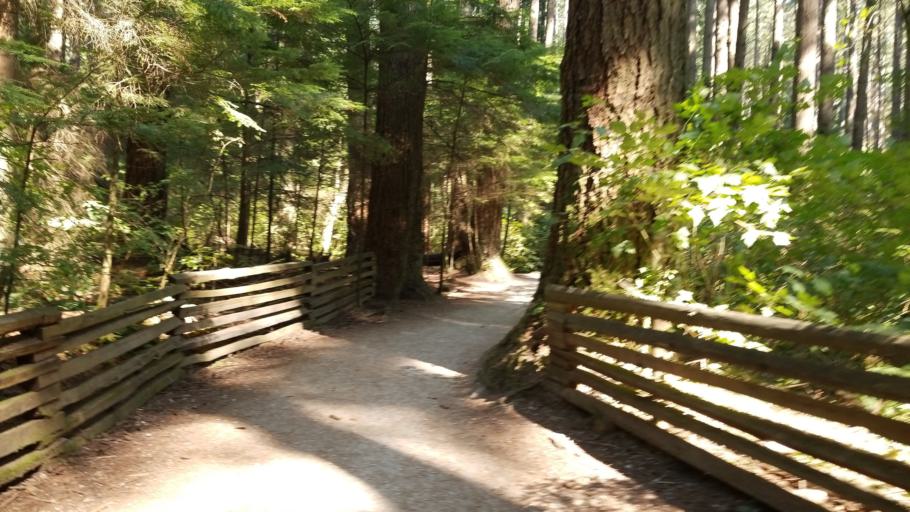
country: CA
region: British Columbia
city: West End
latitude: 49.2522
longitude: -123.2214
